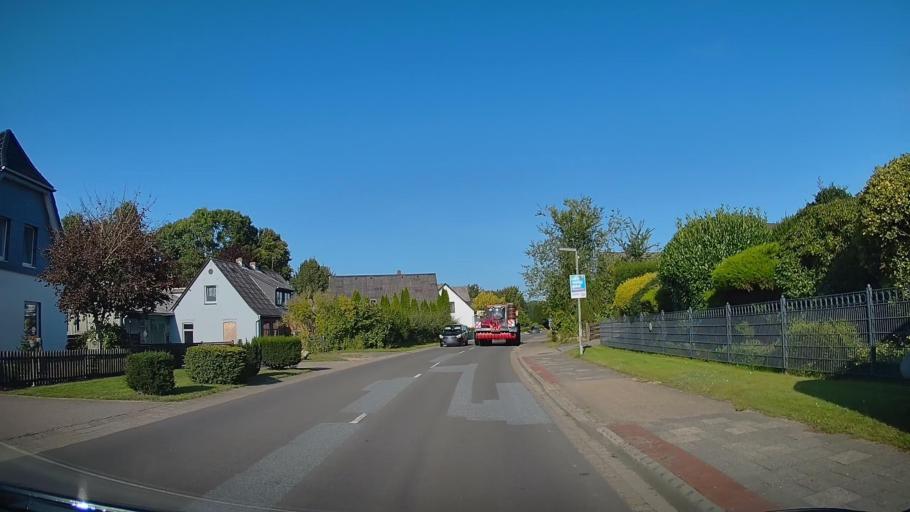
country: DE
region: Lower Saxony
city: Nordholz
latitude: 53.7758
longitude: 8.5889
